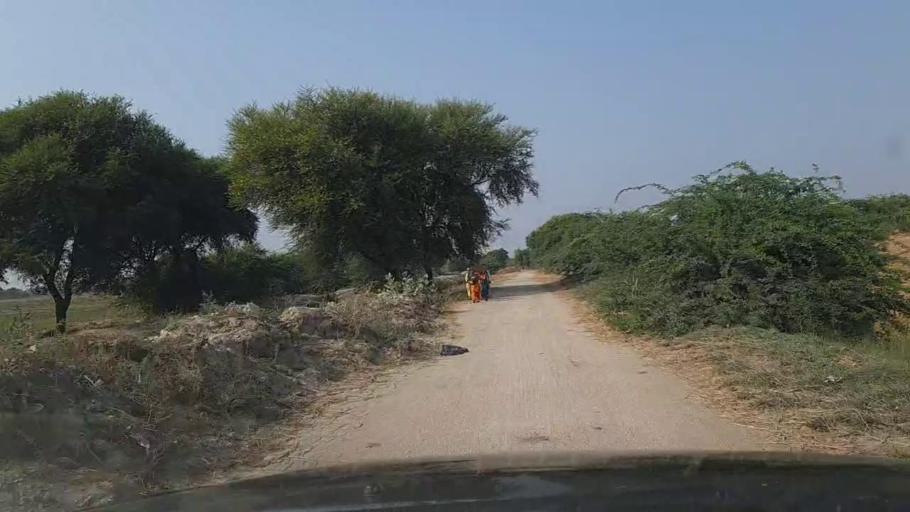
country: PK
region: Sindh
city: Mirpur Batoro
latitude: 24.7031
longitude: 68.2555
